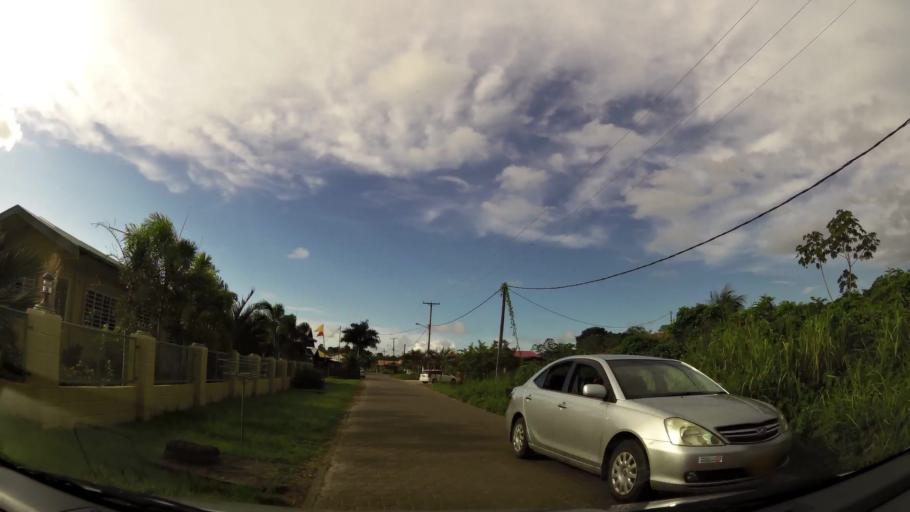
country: SR
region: Paramaribo
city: Paramaribo
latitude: 5.8465
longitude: -55.1778
